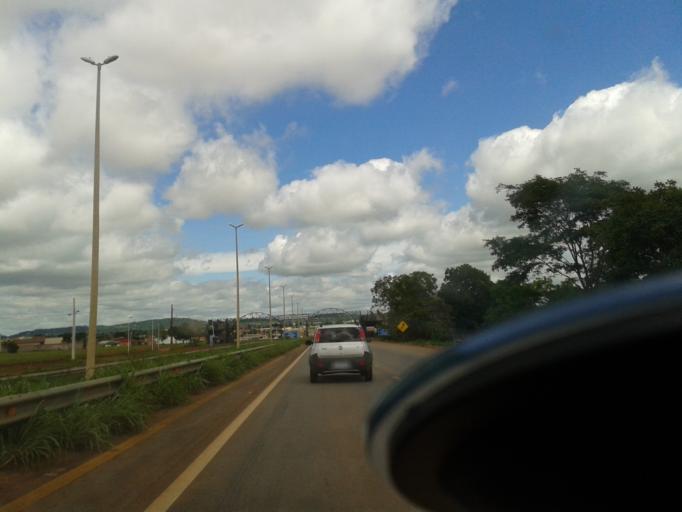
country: BR
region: Goias
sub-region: Goianira
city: Goianira
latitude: -16.5210
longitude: -49.4144
